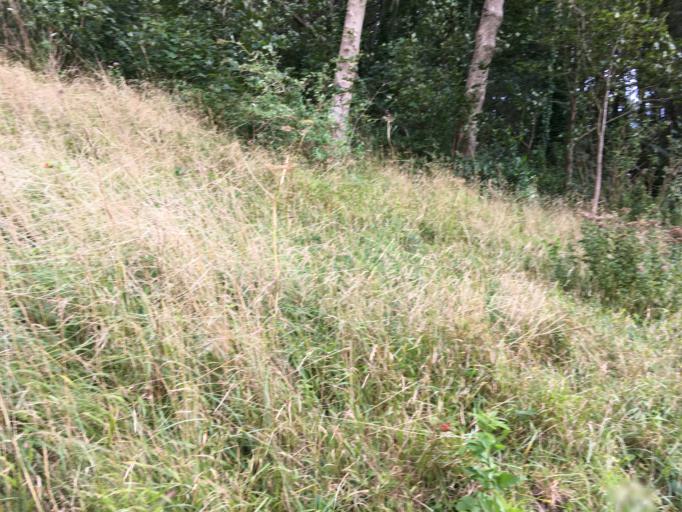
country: GB
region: England
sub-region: Devon
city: Dartmouth
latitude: 50.3466
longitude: -3.5306
